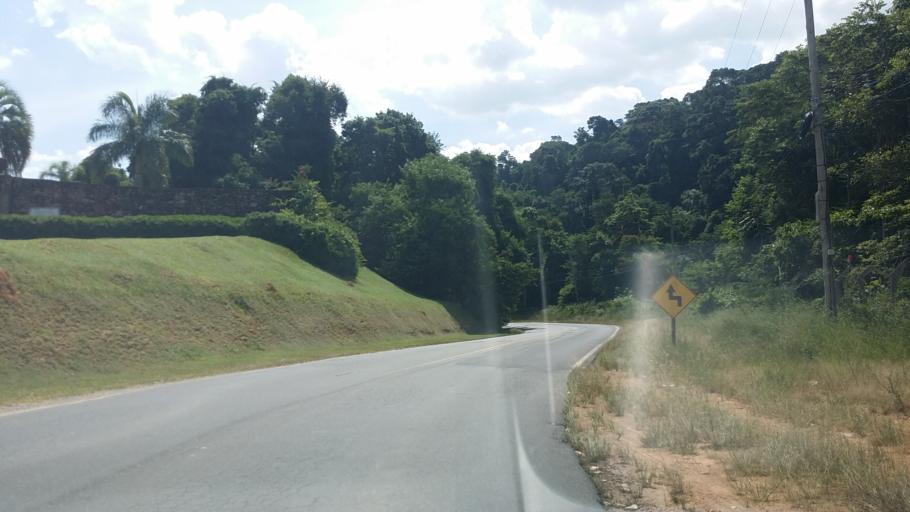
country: BR
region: Sao Paulo
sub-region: Itupeva
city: Itupeva
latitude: -23.1925
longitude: -47.0866
